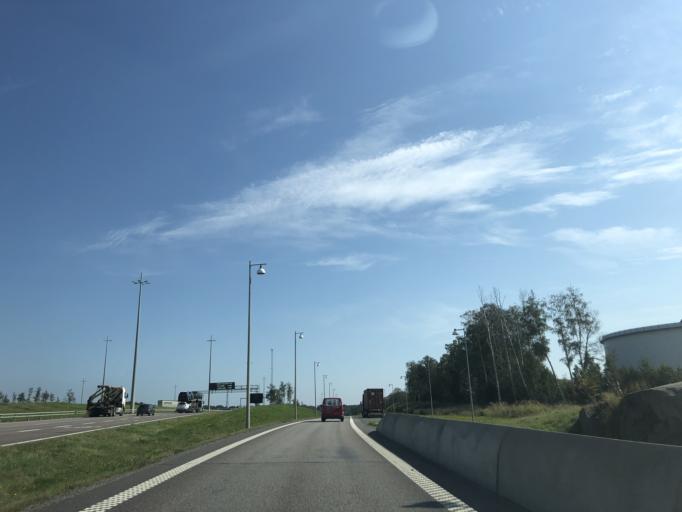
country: SE
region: Vaestra Goetaland
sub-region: Goteborg
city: Majorna
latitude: 57.7044
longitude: 11.8704
